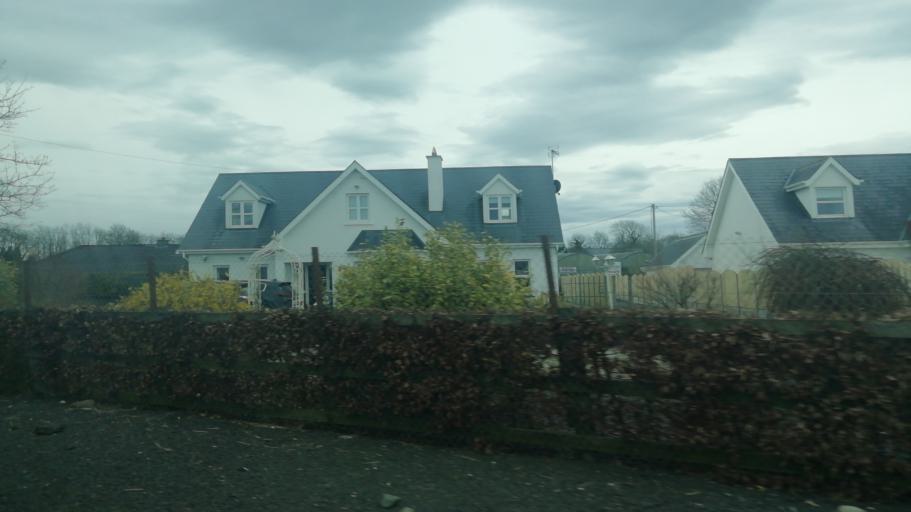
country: IE
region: Leinster
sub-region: Kildare
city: Clane
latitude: 53.3100
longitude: -6.6561
